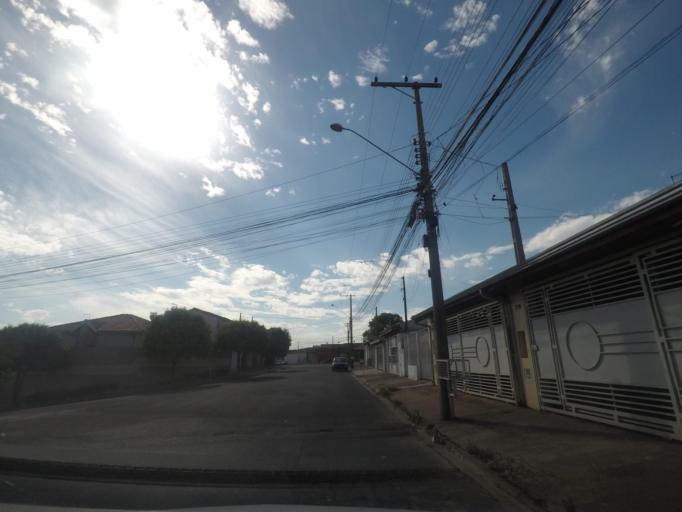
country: BR
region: Sao Paulo
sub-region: Sumare
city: Sumare
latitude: -22.8048
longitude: -47.2705
